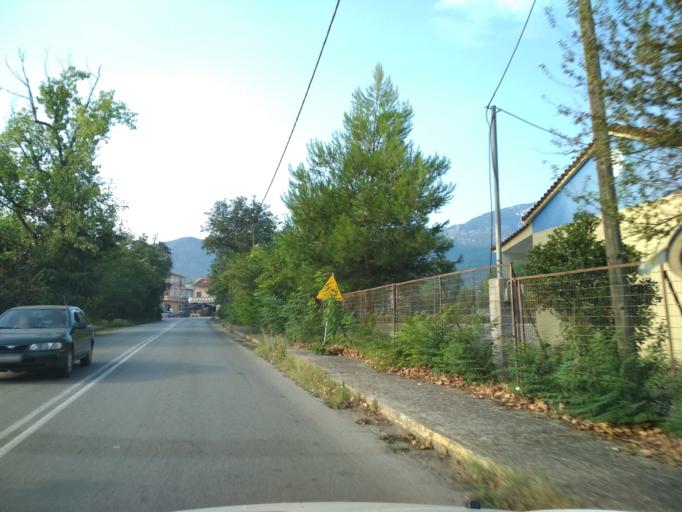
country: GR
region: Central Greece
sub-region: Nomos Evvoias
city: Prokopion
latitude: 38.7361
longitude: 23.4926
